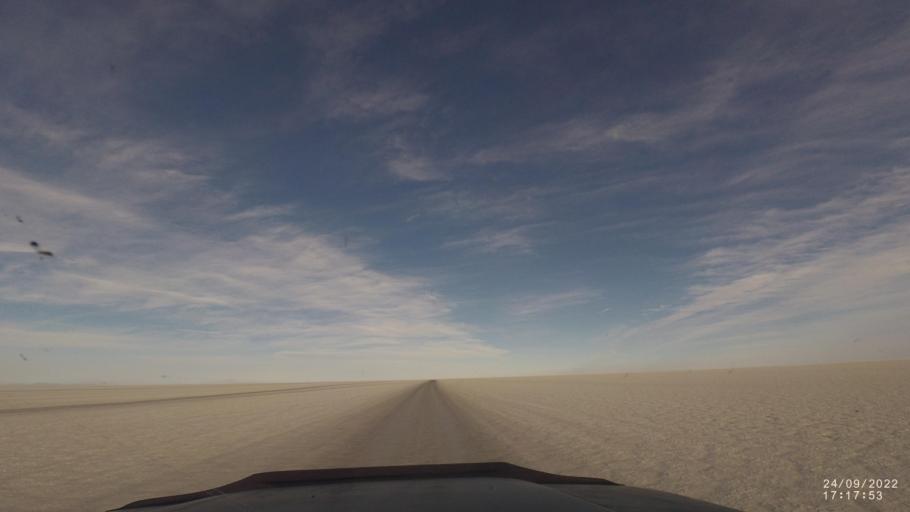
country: BO
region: Potosi
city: Colchani
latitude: -20.2399
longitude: -67.6188
